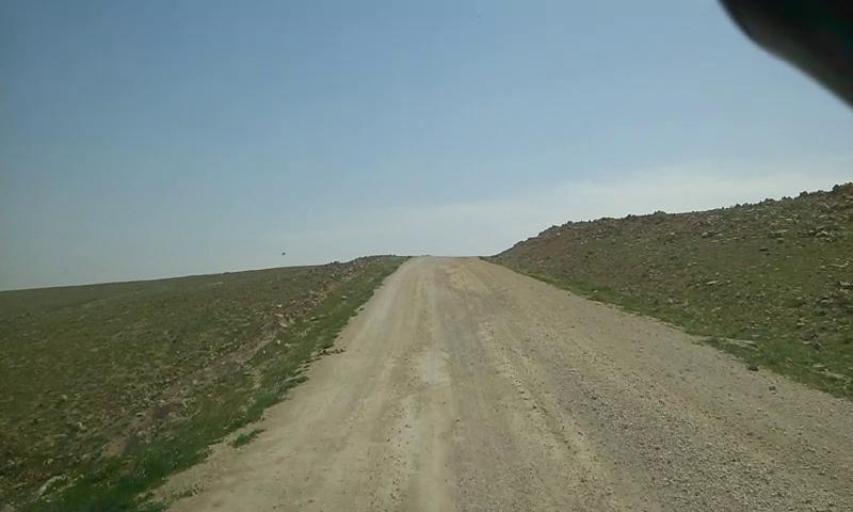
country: PS
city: `Arab ar Rashaydah
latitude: 31.5204
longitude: 35.2970
